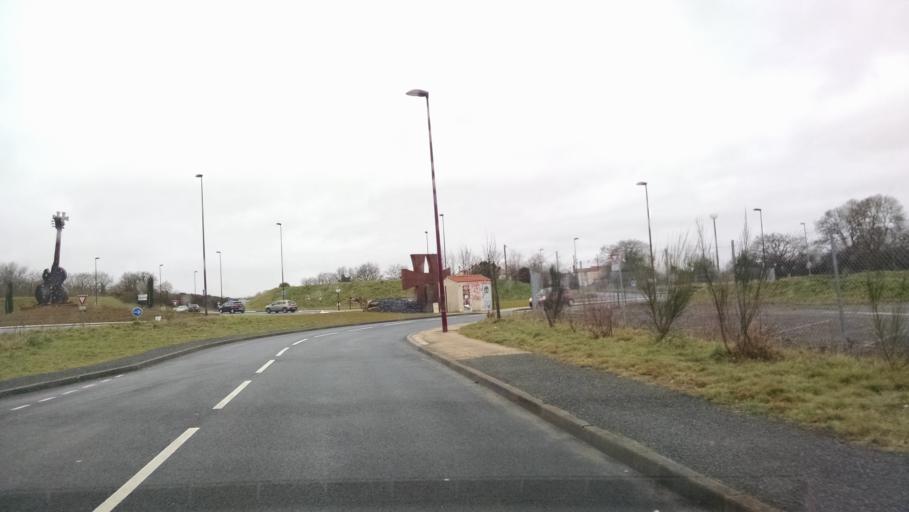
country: FR
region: Pays de la Loire
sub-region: Departement de la Loire-Atlantique
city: Clisson
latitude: 47.0968
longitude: -1.2706
